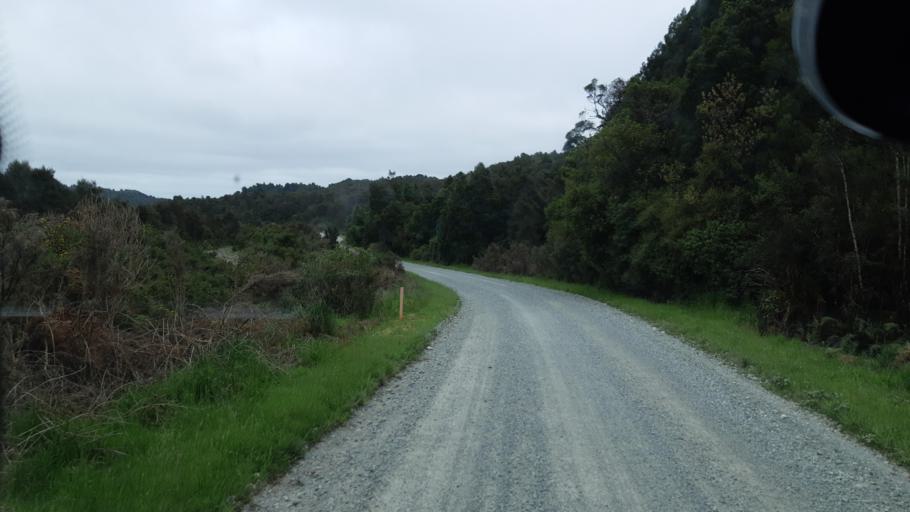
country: NZ
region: West Coast
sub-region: Grey District
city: Greymouth
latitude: -42.6351
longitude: 171.2863
